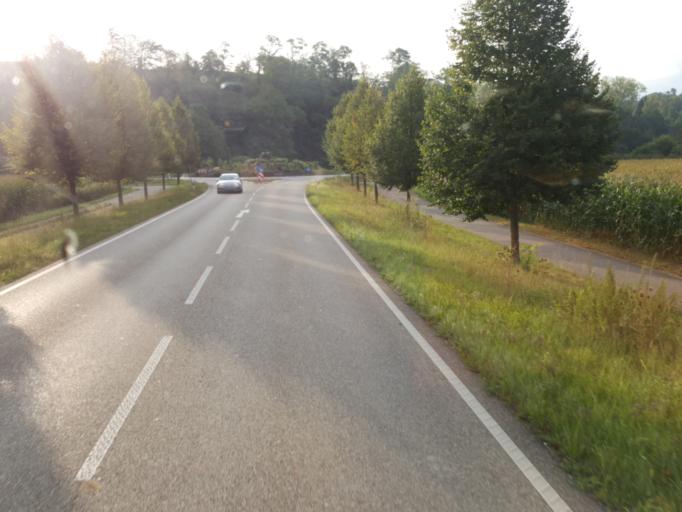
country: DE
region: Baden-Wuerttemberg
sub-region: Freiburg Region
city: Ringsheim
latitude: 48.2526
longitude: 7.7853
